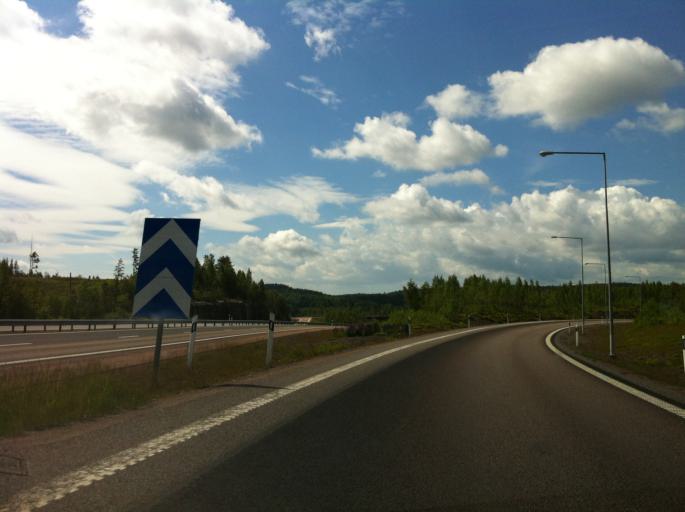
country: SE
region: Vaermland
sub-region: Grums Kommun
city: Slottsbron
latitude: 59.2653
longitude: 13.0074
